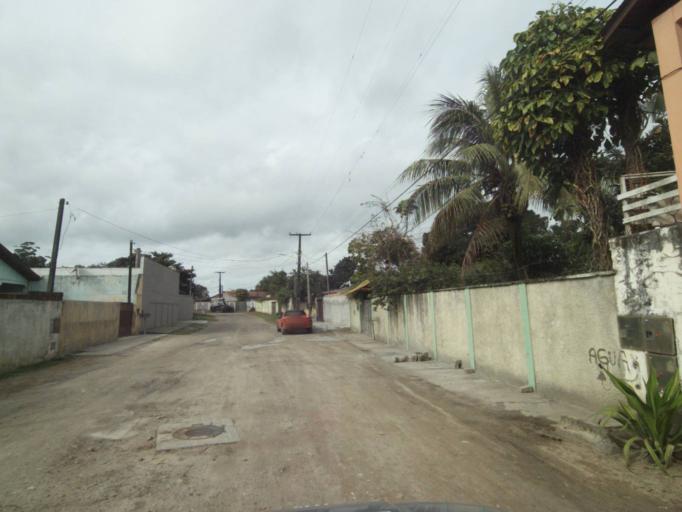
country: BR
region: Parana
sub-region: Paranagua
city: Paranagua
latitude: -25.5692
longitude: -48.5616
